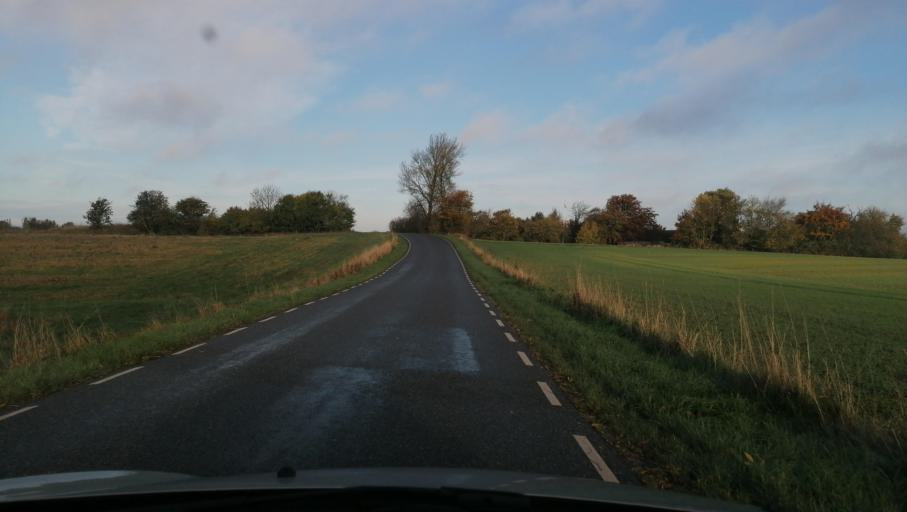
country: DK
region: Zealand
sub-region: Odsherred Kommune
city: Horve
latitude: 55.7497
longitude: 11.3811
